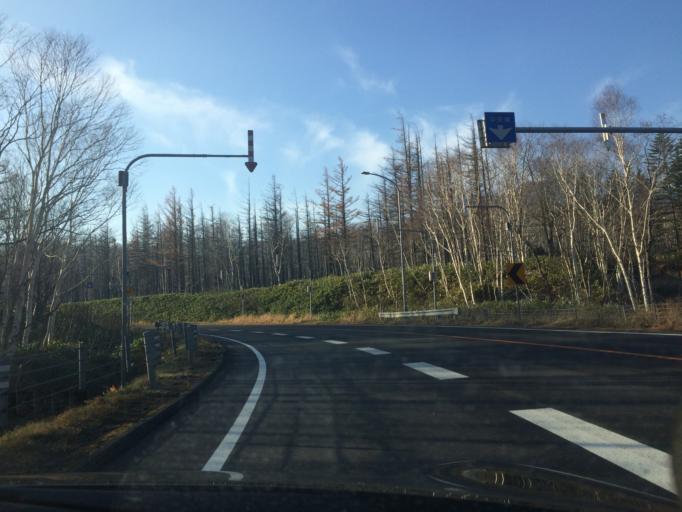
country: JP
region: Hokkaido
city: Otofuke
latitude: 42.9600
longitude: 142.7925
